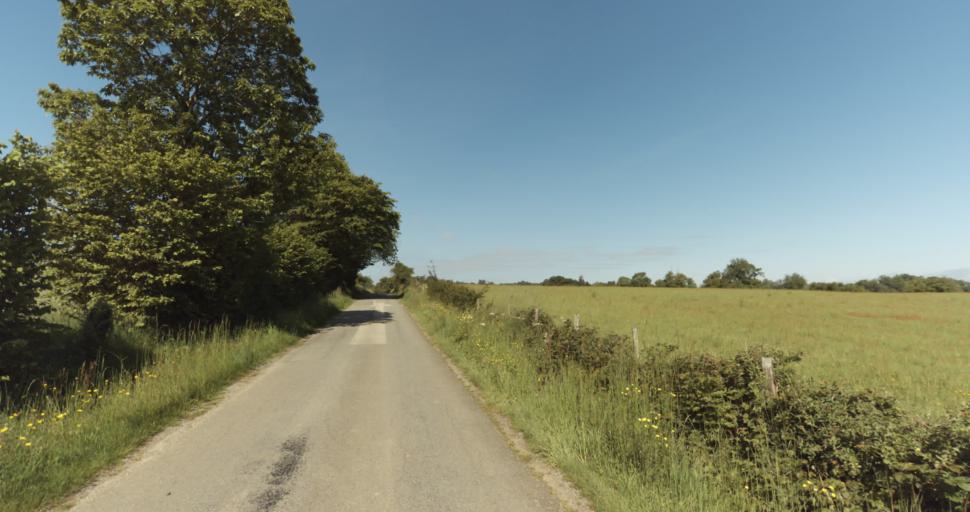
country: FR
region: Limousin
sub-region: Departement de la Haute-Vienne
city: Le Vigen
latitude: 45.7199
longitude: 1.2872
